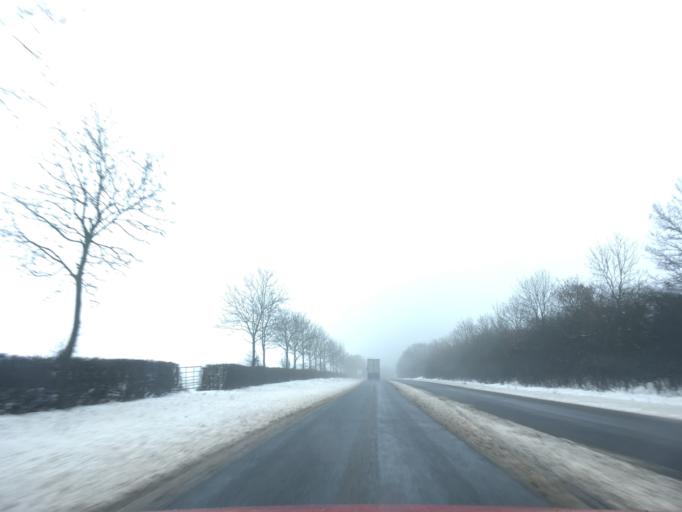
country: GB
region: England
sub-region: Warwickshire
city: Stratford-upon-Avon
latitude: 52.2257
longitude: -1.7022
